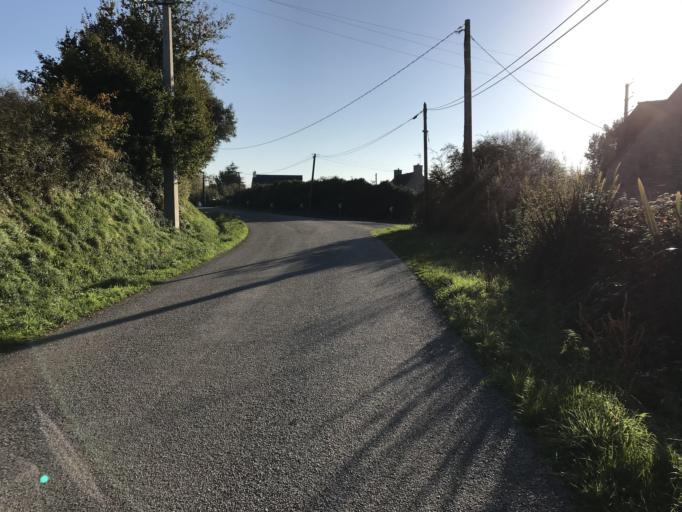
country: FR
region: Brittany
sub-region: Departement du Finistere
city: Hopital-Camfrout
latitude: 48.3022
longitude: -4.2342
